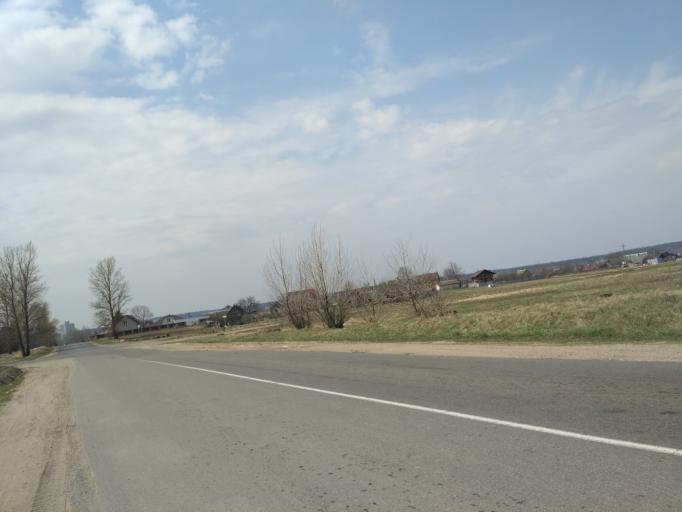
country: BY
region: Minsk
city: Zamostochcha
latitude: 53.8916
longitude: 27.9238
